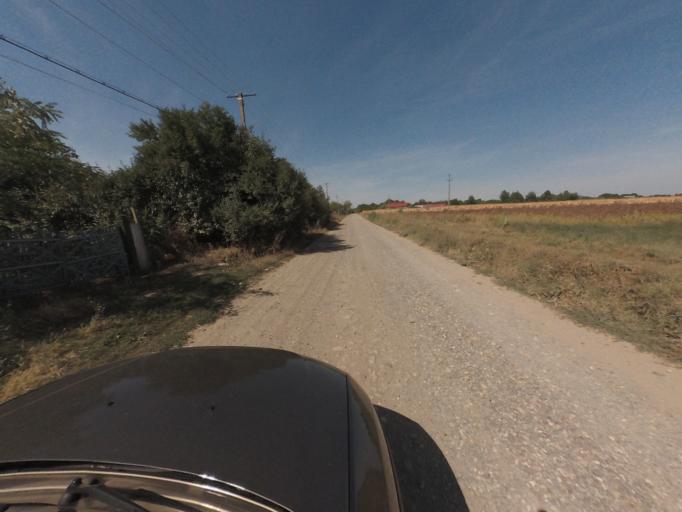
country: RO
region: Vaslui
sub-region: Comuna Deleni
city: Deleni
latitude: 46.5370
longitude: 27.7522
